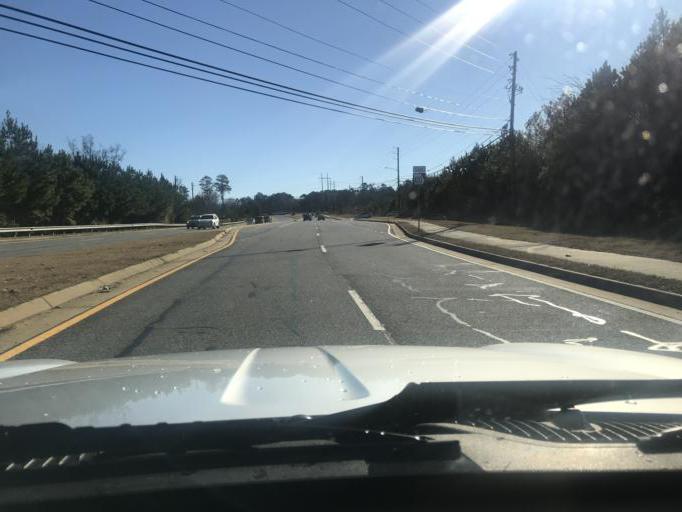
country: US
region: Georgia
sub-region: Gwinnett County
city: Lawrenceville
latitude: 33.9745
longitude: -84.0596
